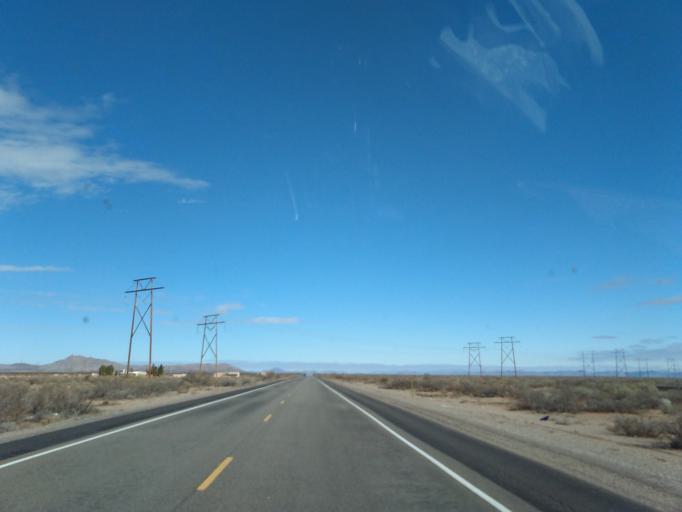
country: US
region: New Mexico
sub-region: Luna County
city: Deming
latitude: 32.3134
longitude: -107.6873
